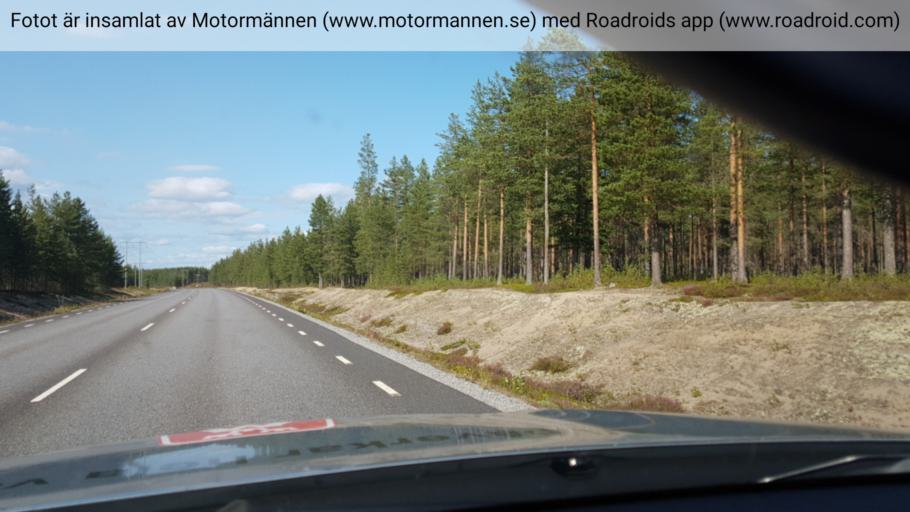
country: SE
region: Norrbotten
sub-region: Pitea Kommun
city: Pitea
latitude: 65.2569
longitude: 21.5385
